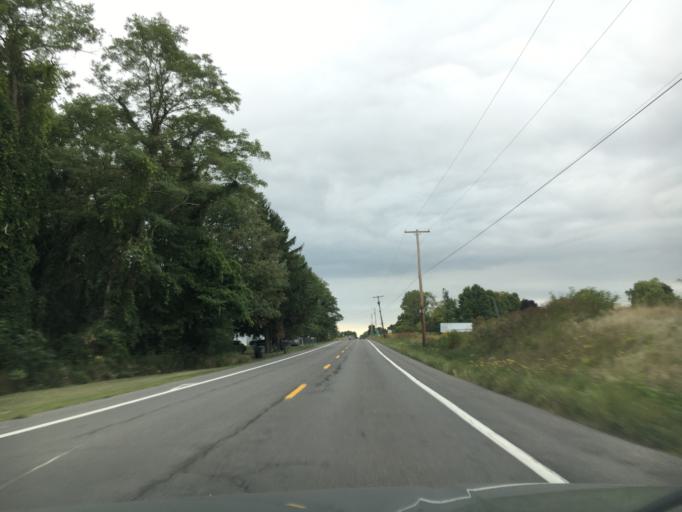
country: US
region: New York
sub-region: Tompkins County
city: Trumansburg
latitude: 42.6627
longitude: -76.7253
